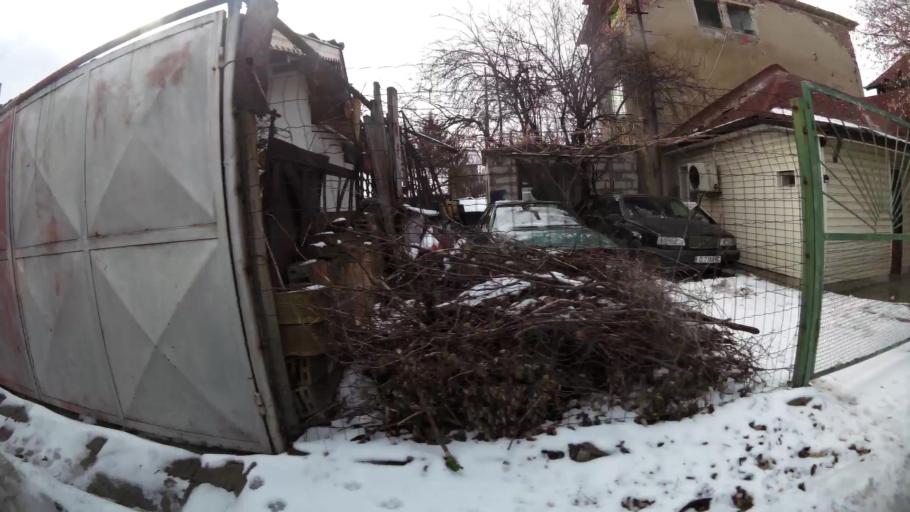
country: BG
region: Sofia-Capital
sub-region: Stolichna Obshtina
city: Sofia
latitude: 42.6988
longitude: 23.3838
